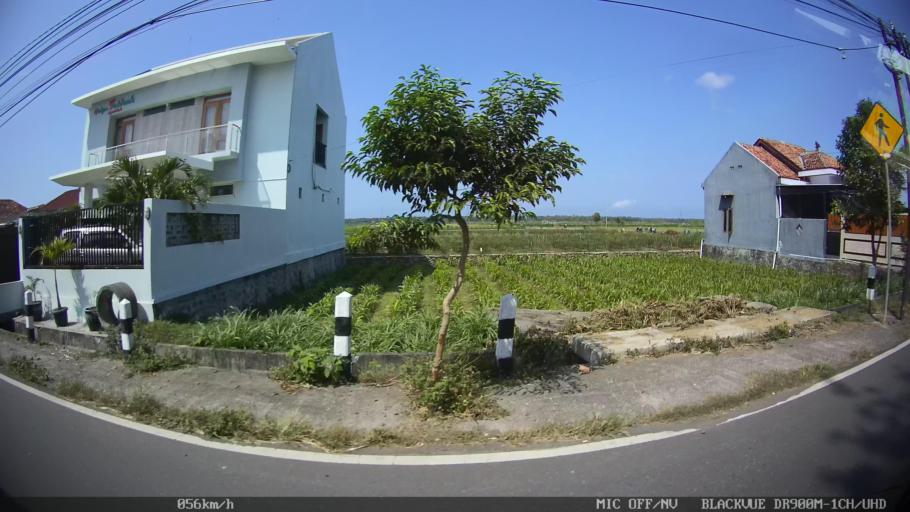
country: ID
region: Daerah Istimewa Yogyakarta
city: Srandakan
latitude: -7.8929
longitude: 110.1351
